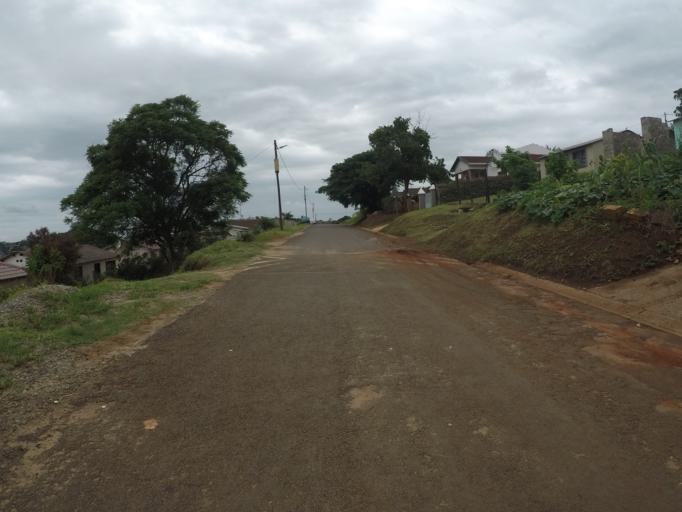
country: ZA
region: KwaZulu-Natal
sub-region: uThungulu District Municipality
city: Empangeni
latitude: -28.7767
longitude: 31.8630
